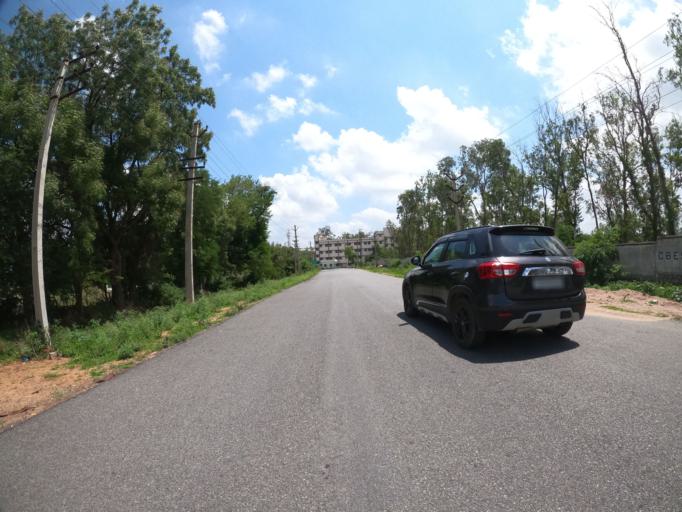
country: IN
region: Telangana
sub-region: Medak
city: Serilingampalle
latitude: 17.3947
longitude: 78.3129
